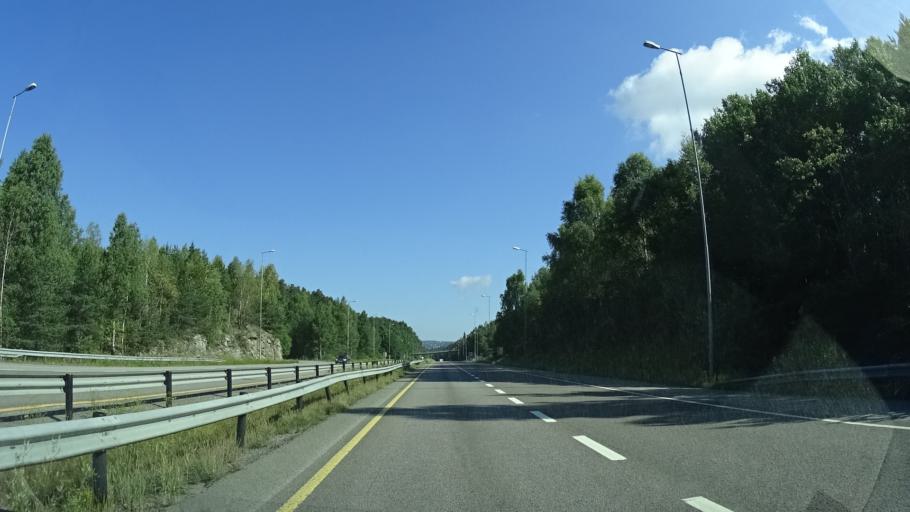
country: NO
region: Akershus
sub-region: Oppegard
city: Kolbotn
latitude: 59.8238
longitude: 10.7763
